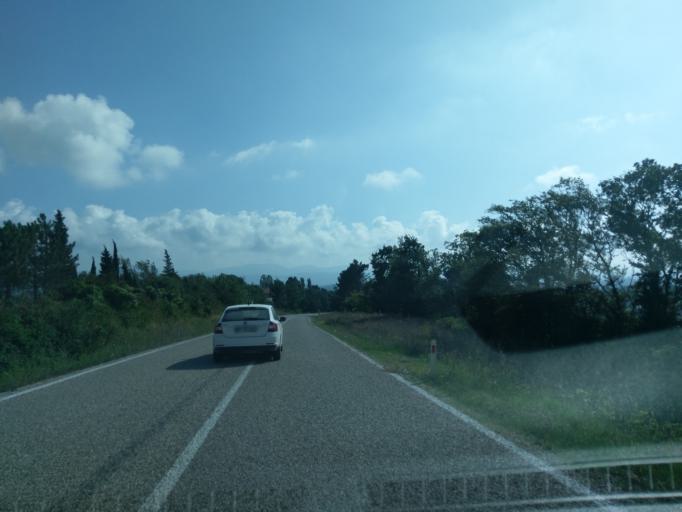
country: TR
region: Sinop
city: Erfelek
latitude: 41.9714
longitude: 34.8634
